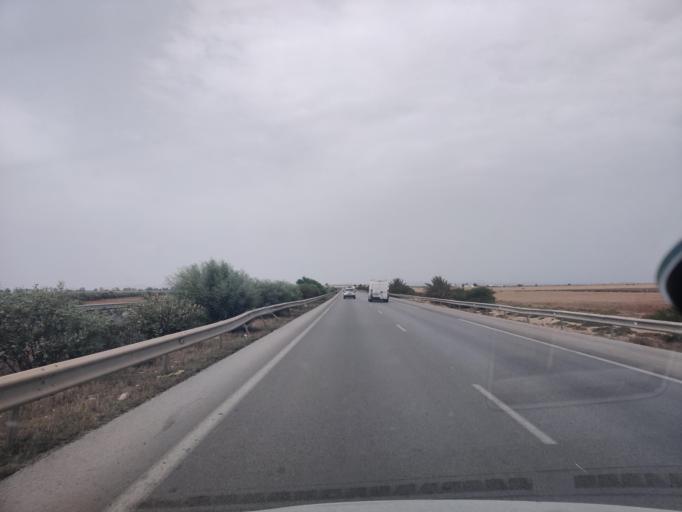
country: TN
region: Susah
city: Harqalah
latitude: 36.0330
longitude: 10.4231
